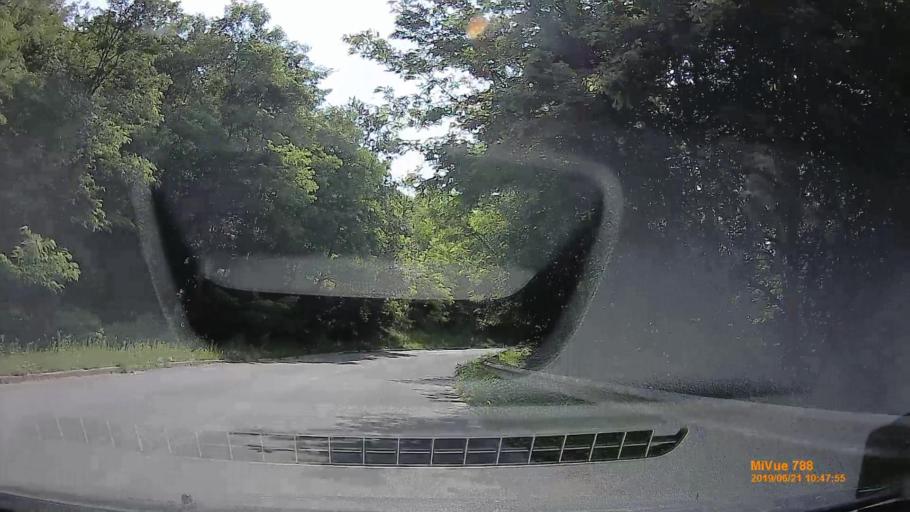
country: HU
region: Baranya
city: Buekkoesd
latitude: 46.1274
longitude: 18.0245
